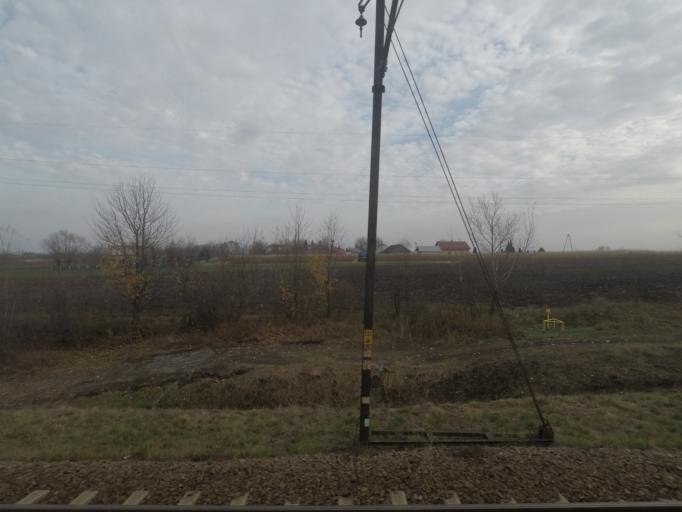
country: PL
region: Subcarpathian Voivodeship
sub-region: Powiat jaroslawski
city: Sosnica
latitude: 49.8649
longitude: 22.8584
